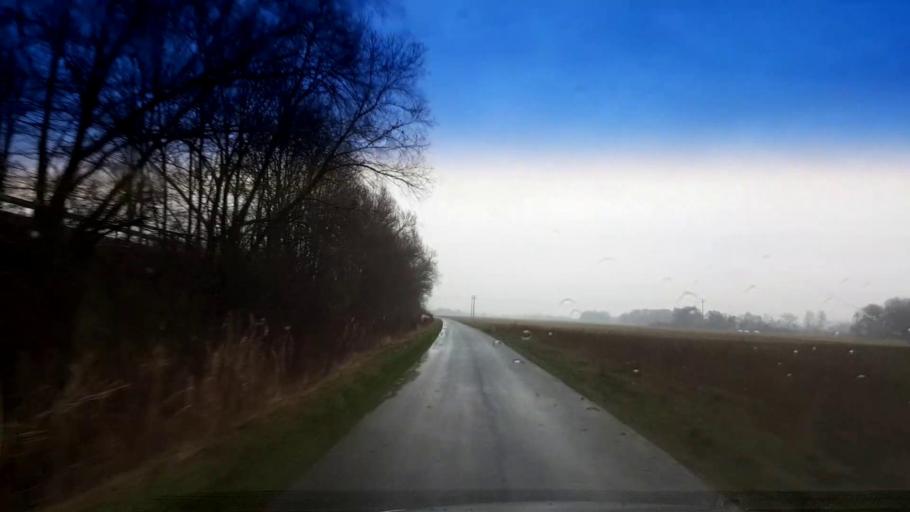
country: DE
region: Bavaria
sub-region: Upper Franconia
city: Viereth-Trunstadt
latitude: 49.9273
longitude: 10.7894
